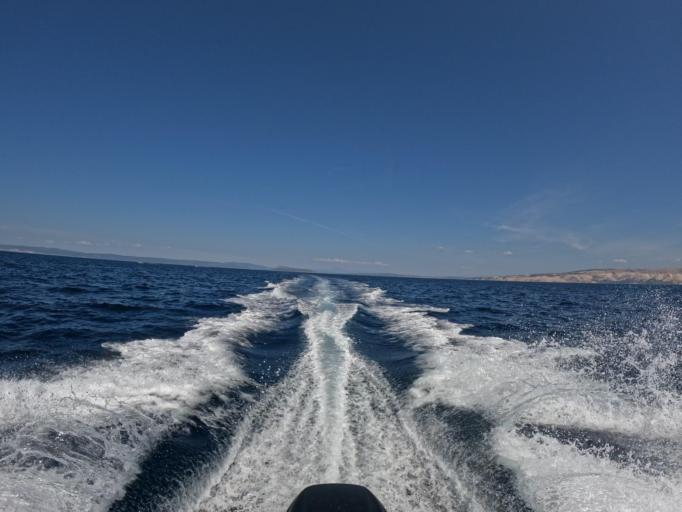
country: HR
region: Primorsko-Goranska
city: Lopar
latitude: 44.8847
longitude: 14.6525
